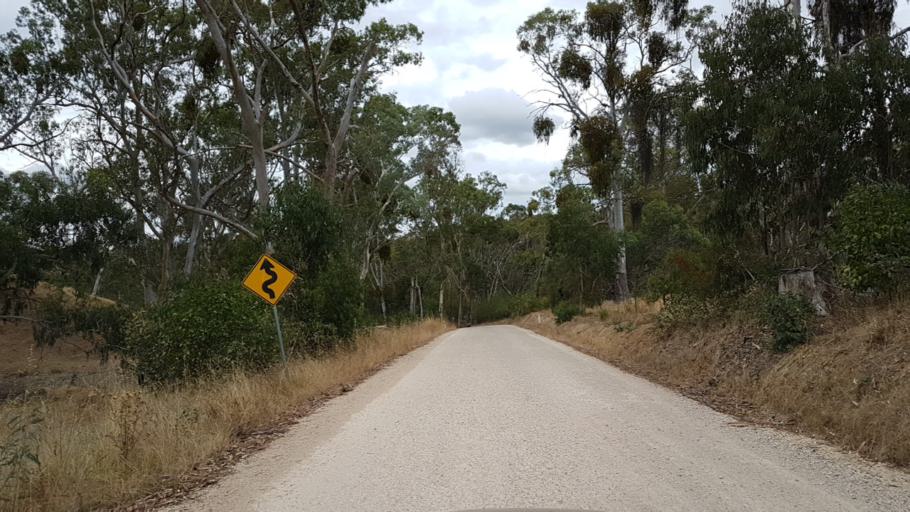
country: AU
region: South Australia
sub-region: Adelaide Hills
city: Gumeracha
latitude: -34.8014
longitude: 138.8243
